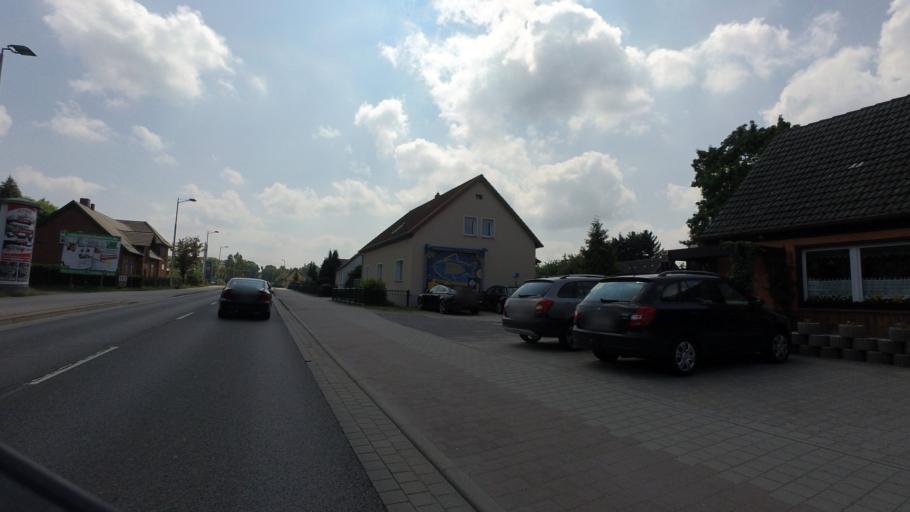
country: DE
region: Brandenburg
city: Cottbus
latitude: 51.7094
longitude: 14.3569
